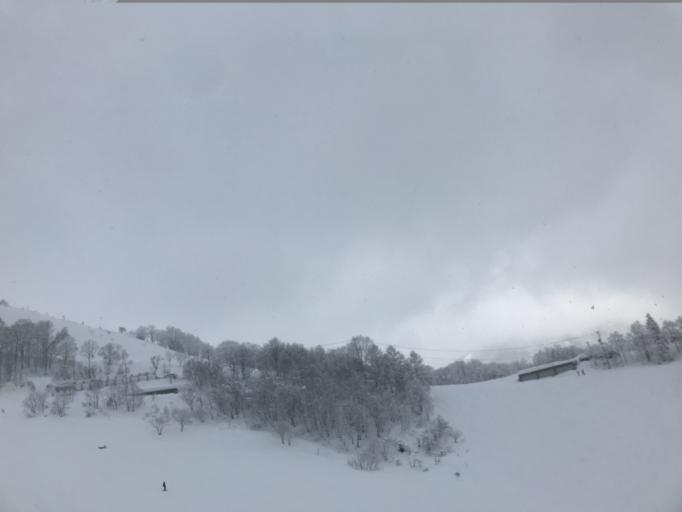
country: JP
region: Nagano
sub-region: Kitaazumi Gun
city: Hakuba
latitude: 36.7072
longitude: 137.8156
